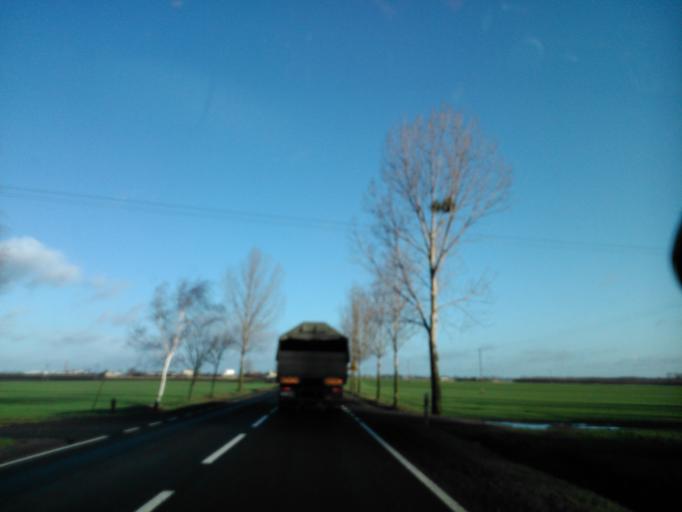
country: PL
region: Kujawsko-Pomorskie
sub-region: Powiat inowroclawski
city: Wierzchoslawice
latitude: 52.8507
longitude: 18.3445
